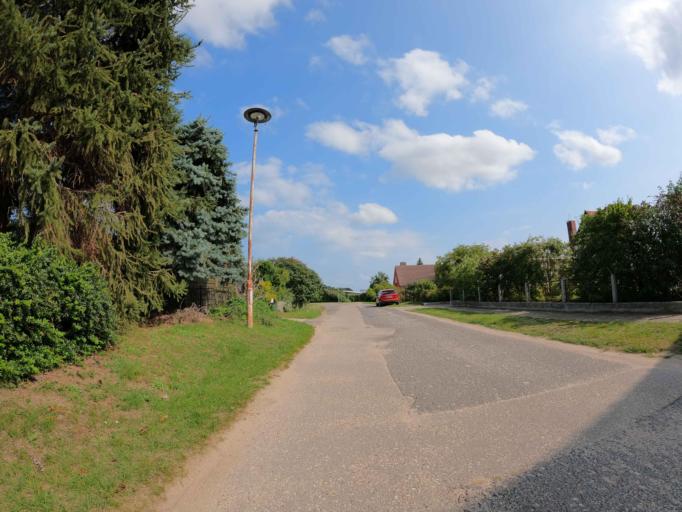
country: DE
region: Mecklenburg-Vorpommern
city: Malchow
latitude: 53.4810
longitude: 12.4366
